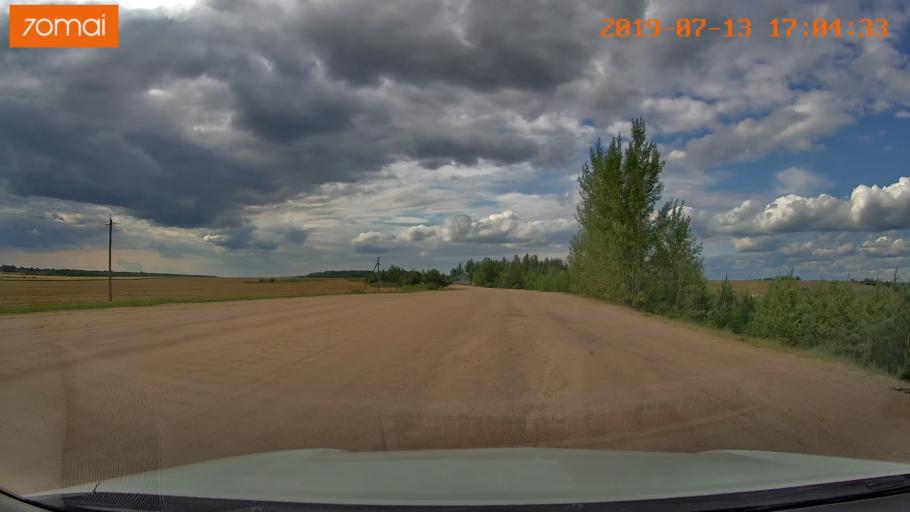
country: BY
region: Mogilev
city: Kirawsk
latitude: 53.2709
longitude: 29.3675
